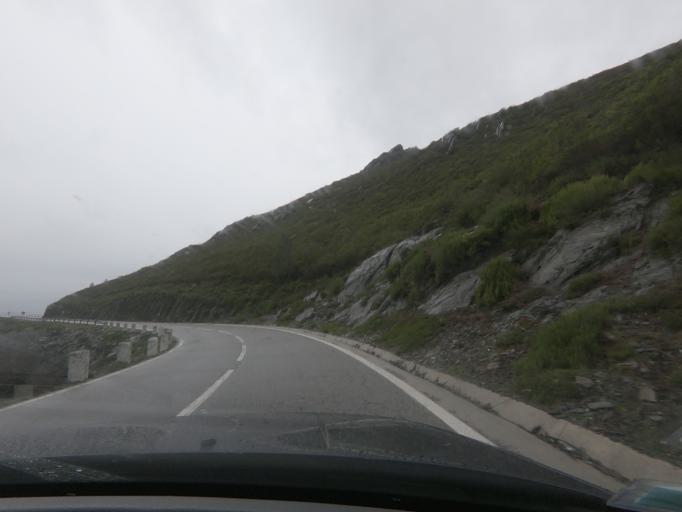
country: PT
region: Vila Real
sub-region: Mondim de Basto
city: Mondim de Basto
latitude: 41.3277
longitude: -7.8755
